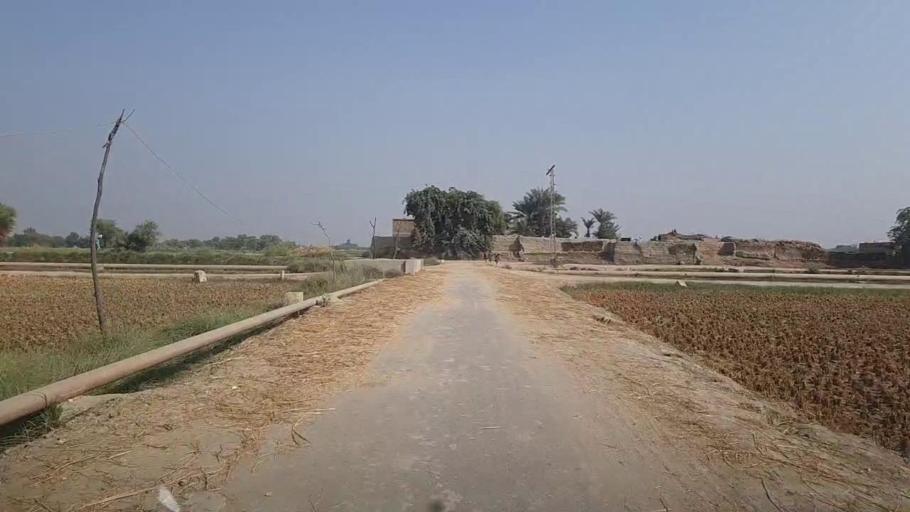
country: PK
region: Sindh
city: Kandhkot
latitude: 28.2337
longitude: 69.2212
